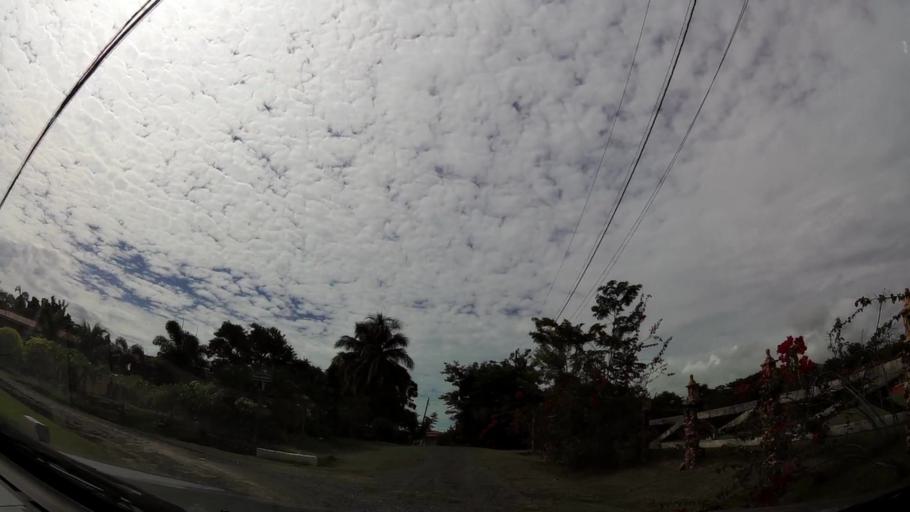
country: PA
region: Panama
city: Nueva Gorgona
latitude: 8.5381
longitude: -79.9046
